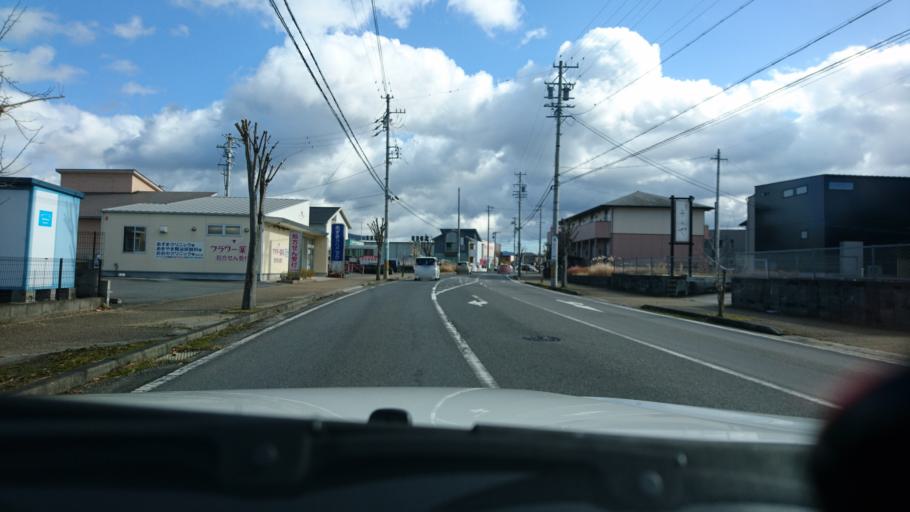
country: JP
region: Mie
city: Ueno-ebisumachi
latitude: 34.7718
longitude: 136.1418
